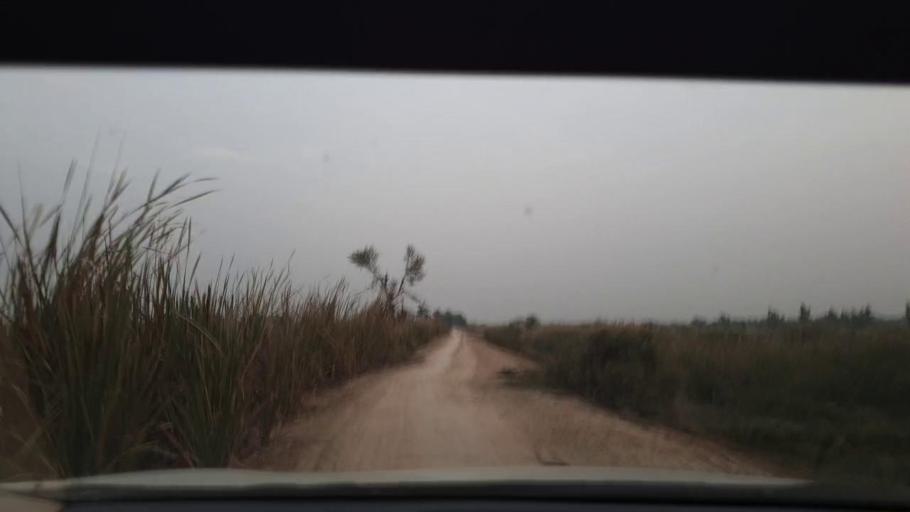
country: PK
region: Sindh
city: Berani
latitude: 25.8525
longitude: 68.7819
